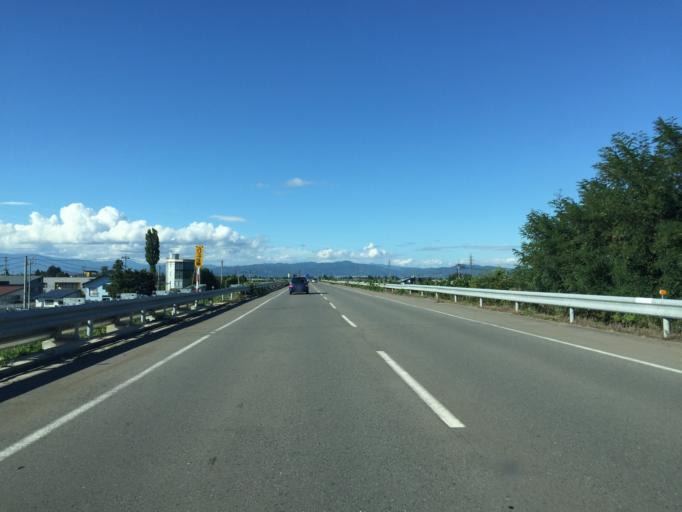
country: JP
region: Yamagata
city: Yonezawa
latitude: 37.9457
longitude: 140.1120
